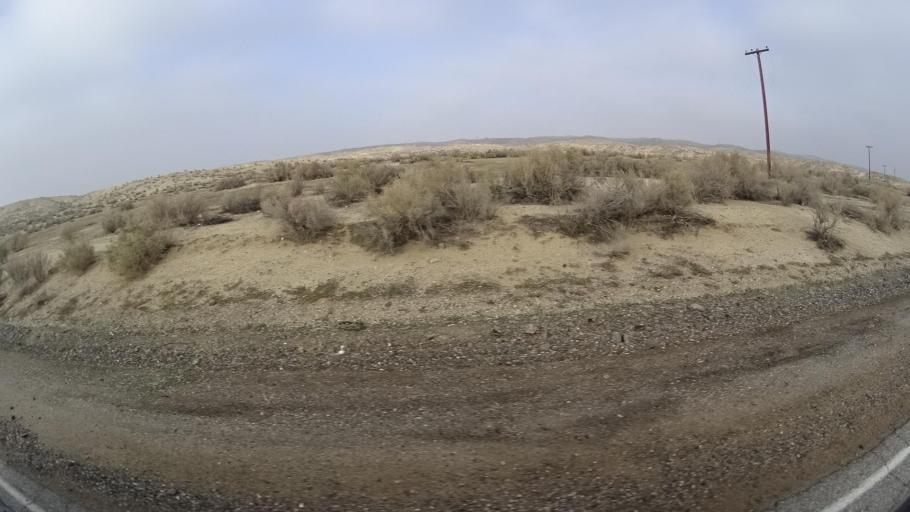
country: US
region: California
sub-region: Kern County
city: South Taft
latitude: 35.1356
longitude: -119.4078
